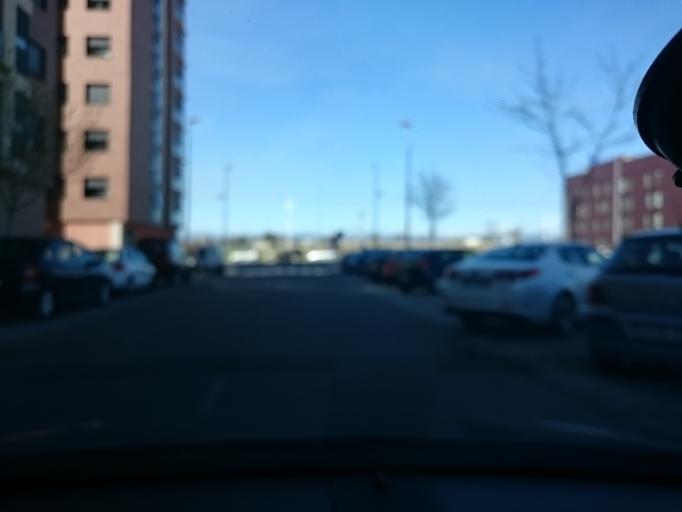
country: ES
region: Castille and Leon
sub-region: Provincia de Leon
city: Ponferrada
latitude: 42.5574
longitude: -6.6099
